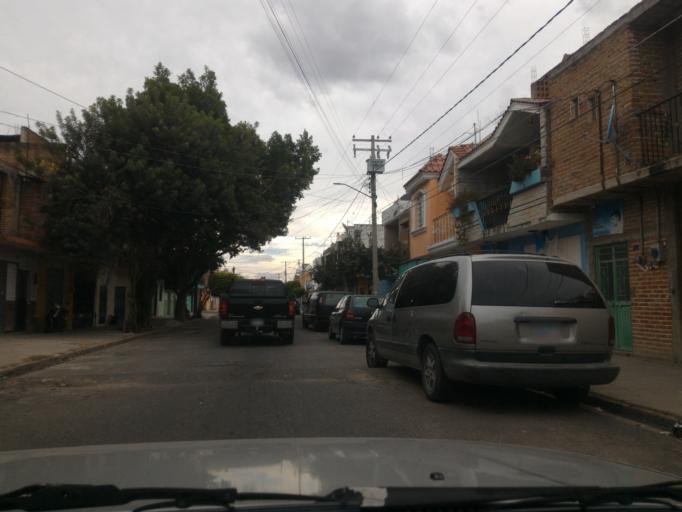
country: MX
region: Guanajuato
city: San Francisco del Rincon
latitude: 21.0277
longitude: -101.8623
